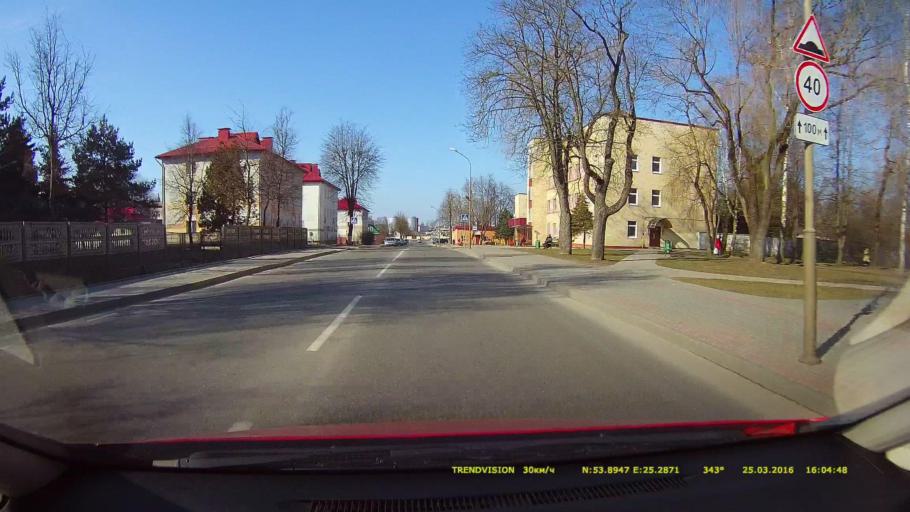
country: BY
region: Grodnenskaya
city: Lida
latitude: 53.8949
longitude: 25.2870
